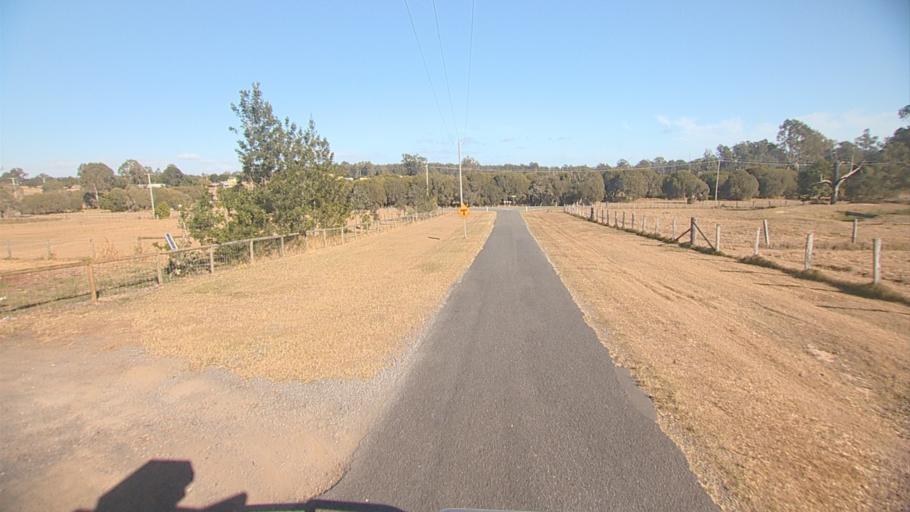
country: AU
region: Queensland
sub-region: Logan
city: Cedar Vale
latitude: -27.8470
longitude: 153.0097
